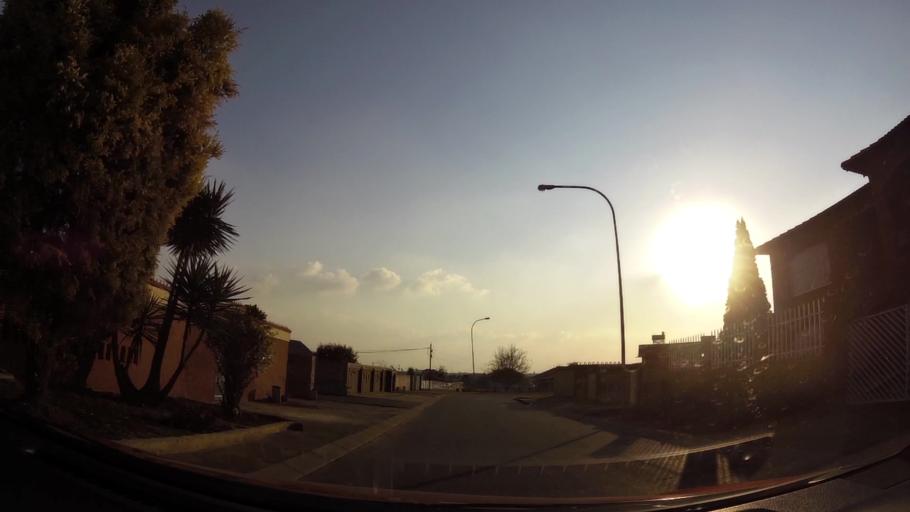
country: ZA
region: Gauteng
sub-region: City of Johannesburg Metropolitan Municipality
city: Soweto
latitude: -26.2859
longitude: 27.8951
